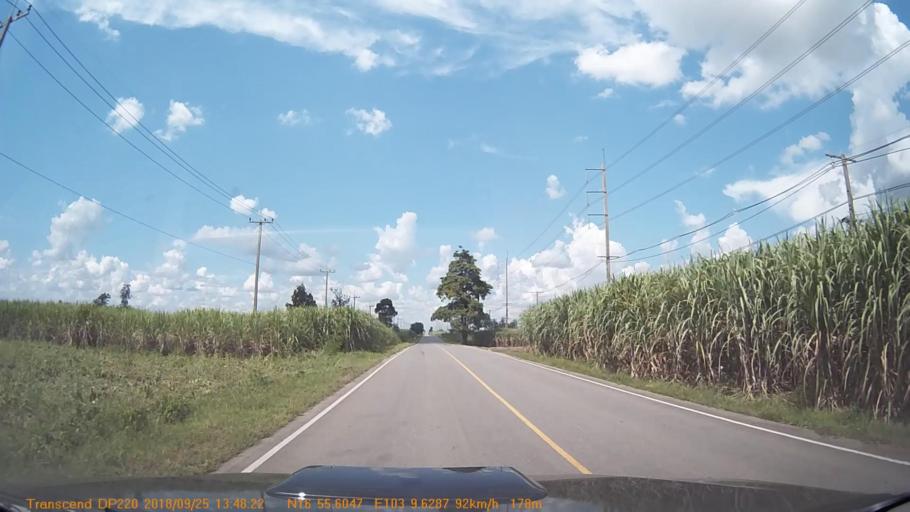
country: TH
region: Changwat Udon Thani
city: Si That
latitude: 16.9269
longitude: 103.1605
